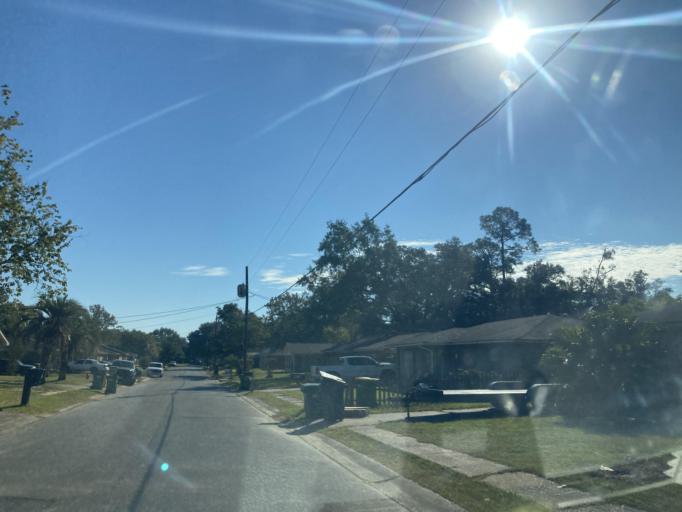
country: US
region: Mississippi
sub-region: Jackson County
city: Saint Martin
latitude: 30.4443
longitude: -88.8779
